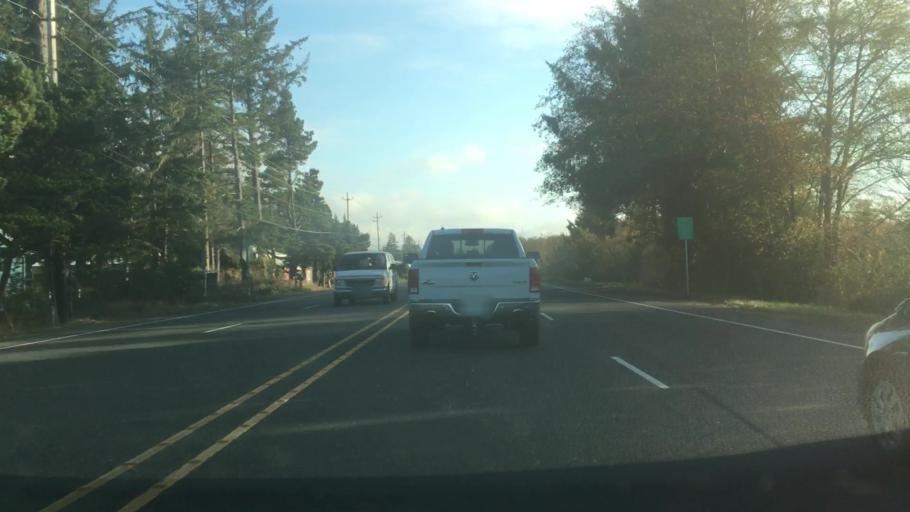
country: US
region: Oregon
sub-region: Clatsop County
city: Gearhart
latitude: 46.0303
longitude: -123.9126
